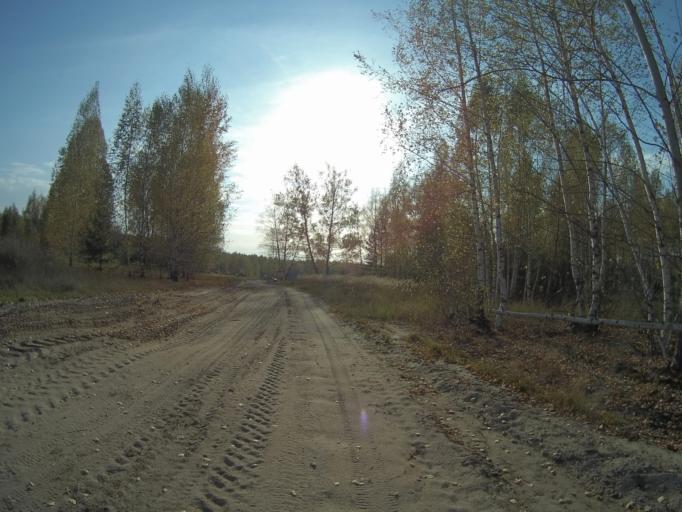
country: RU
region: Vladimir
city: Urshel'skiy
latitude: 55.8109
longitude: 40.1554
